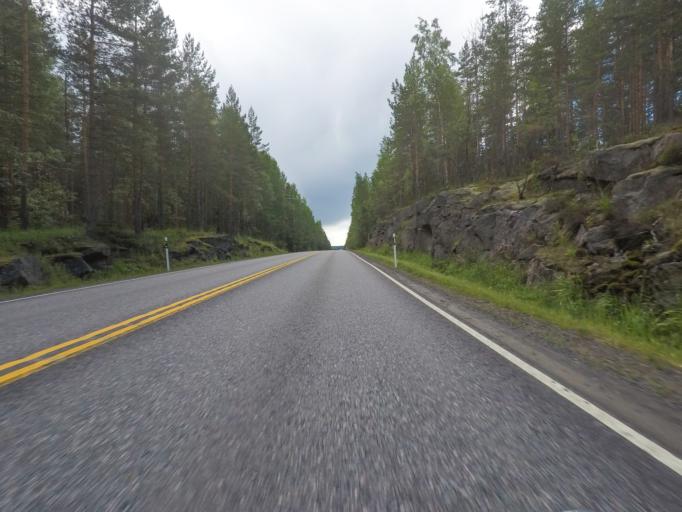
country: FI
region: Paijanne Tavastia
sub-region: Lahti
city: Hartola
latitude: 61.6652
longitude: 26.0340
